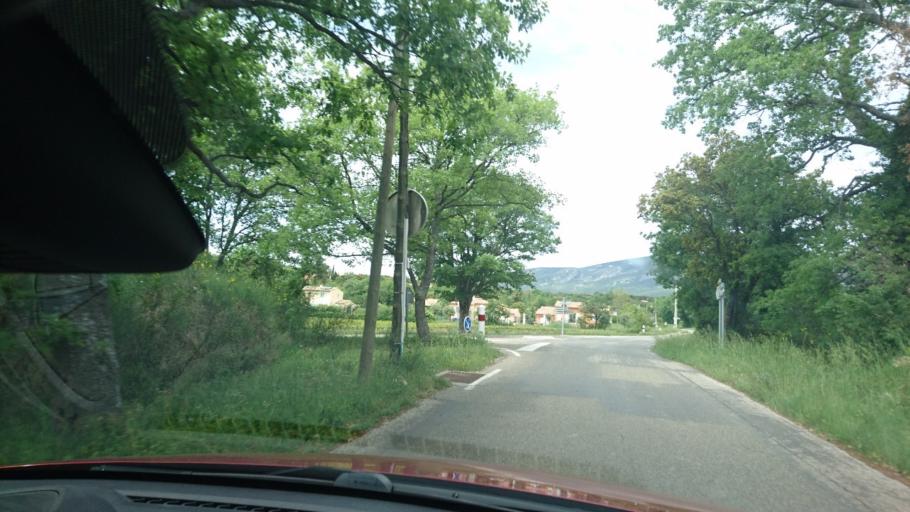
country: FR
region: Provence-Alpes-Cote d'Azur
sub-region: Departement du Vaucluse
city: Villes-sur-Auzon
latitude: 44.0930
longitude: 5.2393
